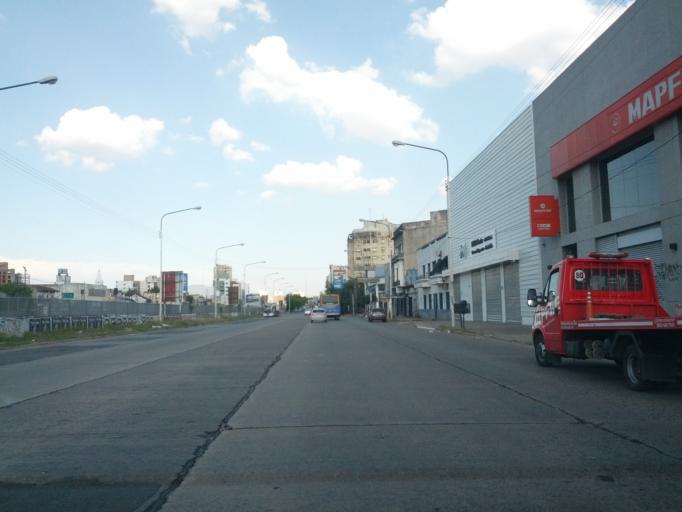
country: AR
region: Buenos Aires
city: San Justo
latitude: -34.6401
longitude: -58.5477
